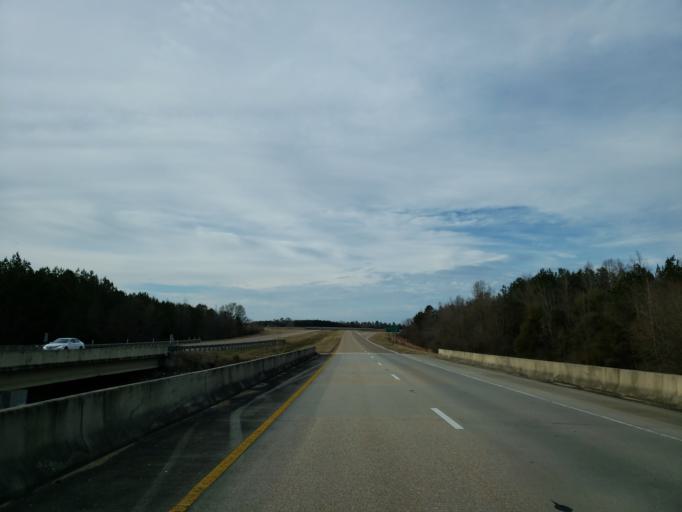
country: US
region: Mississippi
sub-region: Wayne County
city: Waynesboro
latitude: 31.6757
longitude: -88.6101
